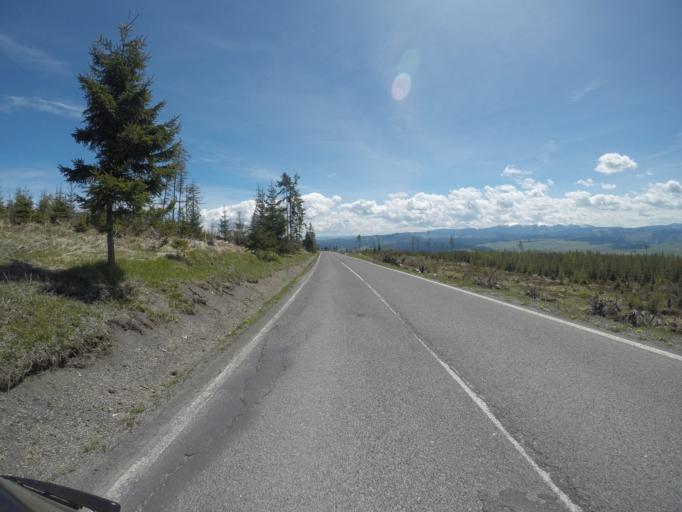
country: SK
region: Presovsky
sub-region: Okres Poprad
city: Strba
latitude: 49.1094
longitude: 20.0697
